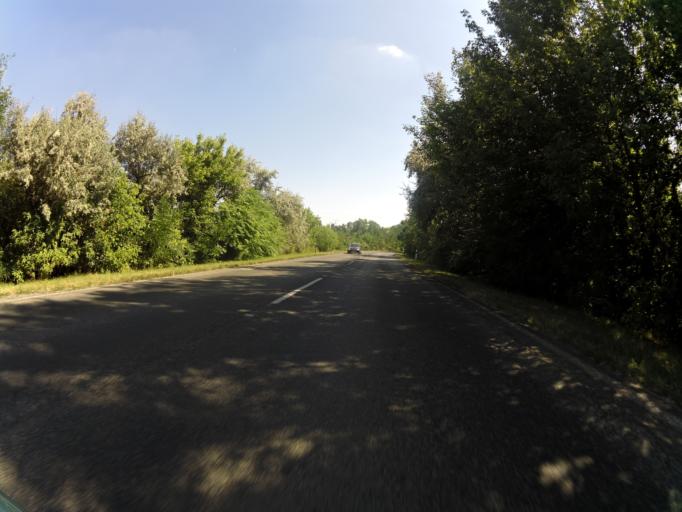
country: HU
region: Csongrad
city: Szatymaz
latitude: 46.3389
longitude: 20.0659
